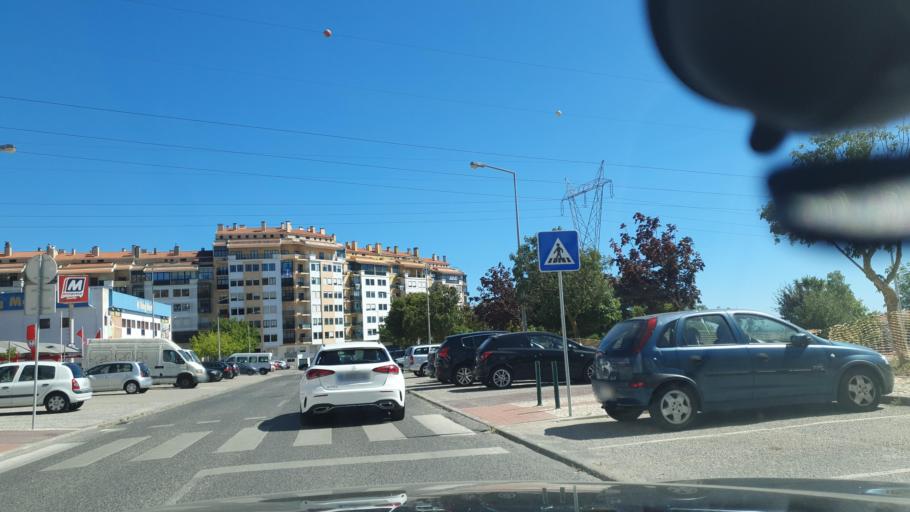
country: PT
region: Lisbon
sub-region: Sintra
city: Cacem
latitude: 38.7630
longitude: -9.2774
